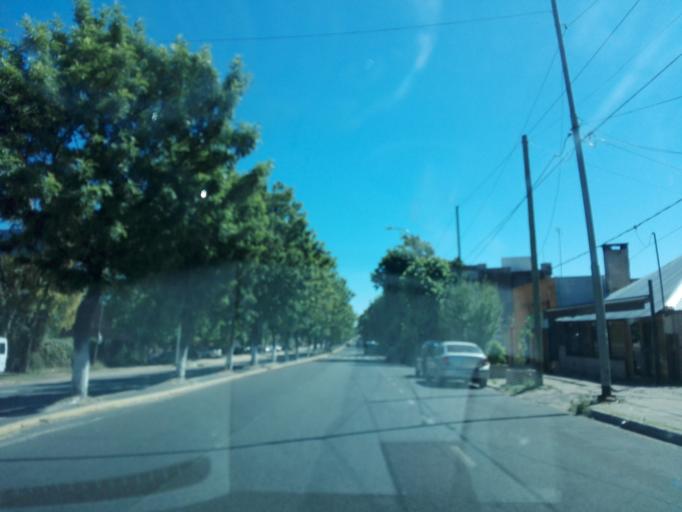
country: AR
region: Buenos Aires
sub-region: Partido de La Plata
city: La Plata
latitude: -34.9071
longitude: -57.9262
